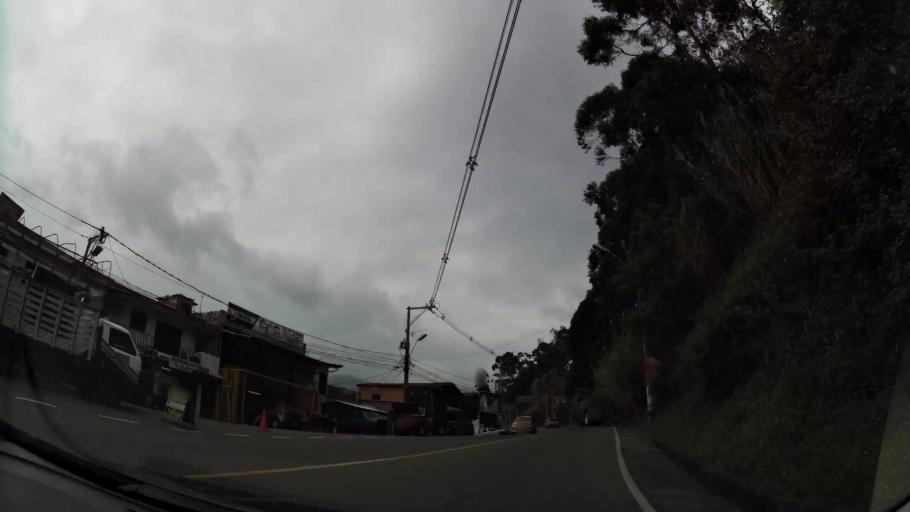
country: CO
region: Antioquia
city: Medellin
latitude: 6.2769
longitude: -75.6178
